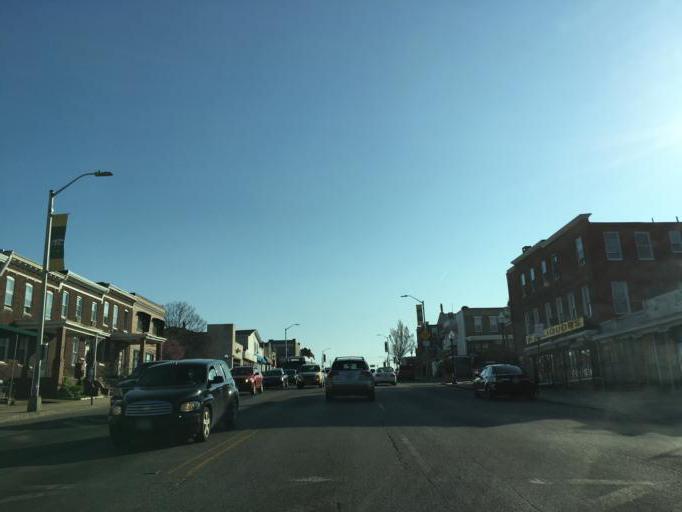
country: US
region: Maryland
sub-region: Baltimore County
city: Rosedale
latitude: 39.3247
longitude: -76.5698
